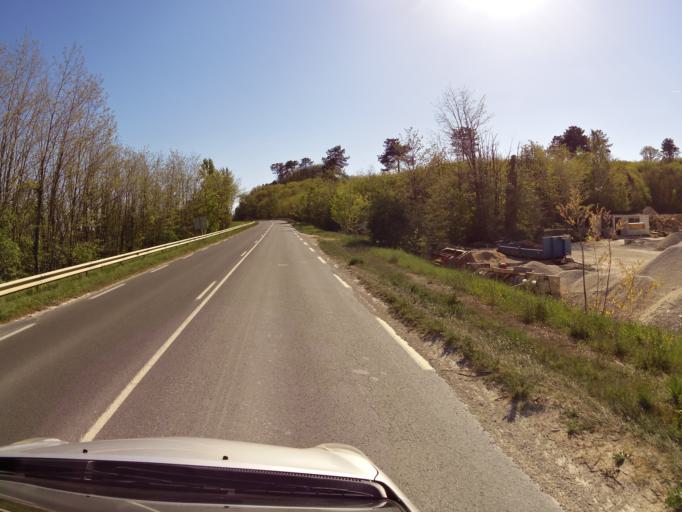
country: FR
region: Aquitaine
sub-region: Departement de la Dordogne
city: Sarlat-la-Caneda
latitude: 44.9427
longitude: 1.2179
